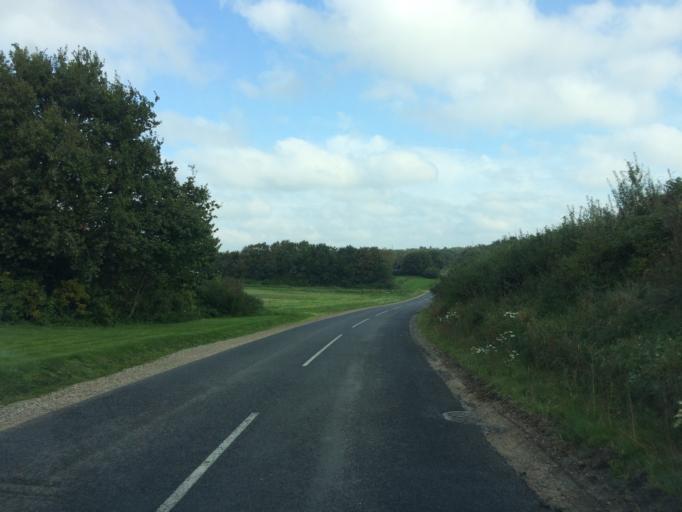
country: DK
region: Central Jutland
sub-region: Holstebro Kommune
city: Vinderup
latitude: 56.4611
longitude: 8.8808
